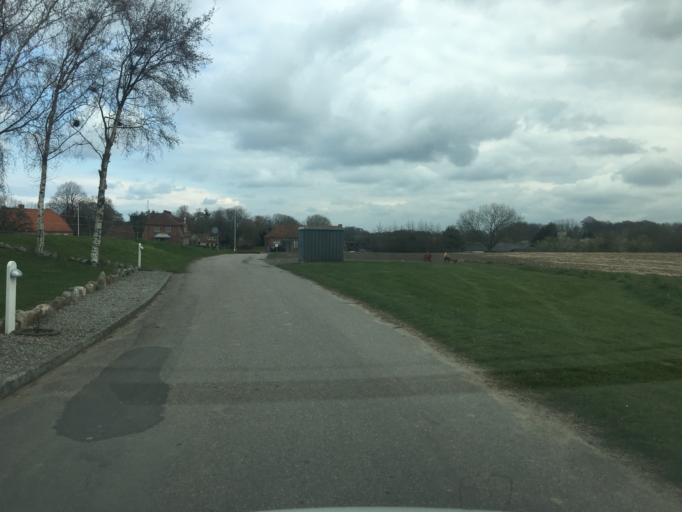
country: DK
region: South Denmark
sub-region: Sonderborg Kommune
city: Grasten
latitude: 55.0054
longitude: 9.5438
